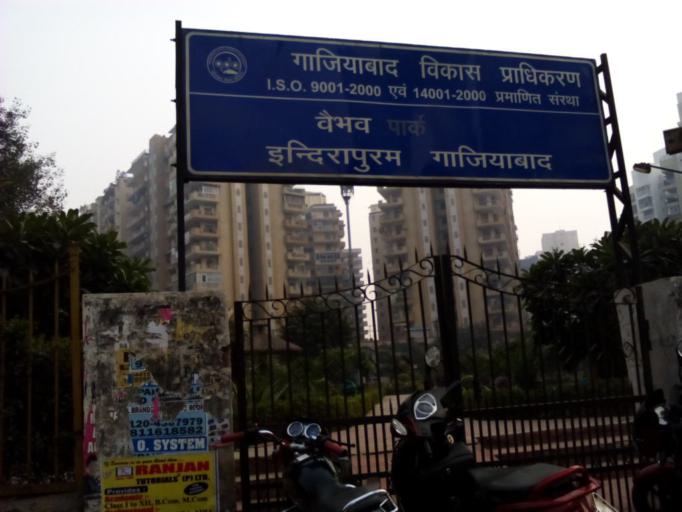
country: IN
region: Uttar Pradesh
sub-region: Gautam Buddha Nagar
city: Noida
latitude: 28.6370
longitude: 77.3631
